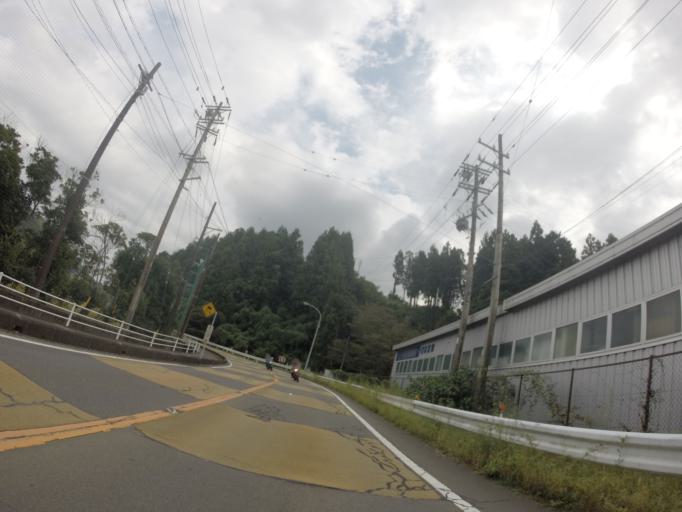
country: JP
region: Shizuoka
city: Fujieda
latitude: 34.8951
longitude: 138.2102
